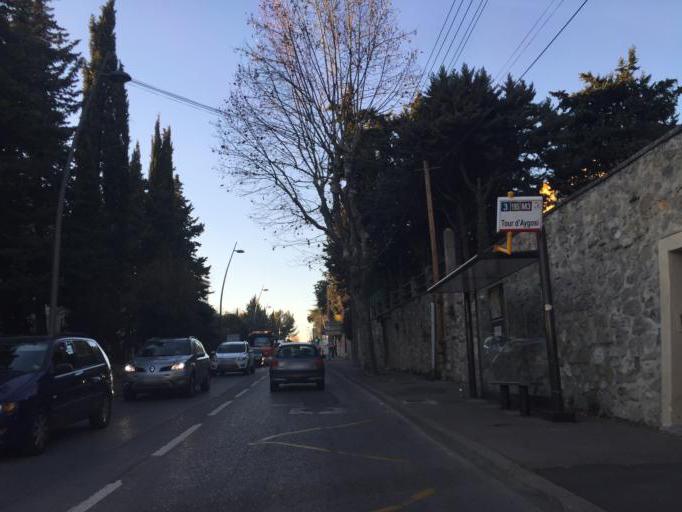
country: FR
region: Provence-Alpes-Cote d'Azur
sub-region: Departement des Bouches-du-Rhone
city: Aix-en-Provence
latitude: 43.5195
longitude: 5.4616
